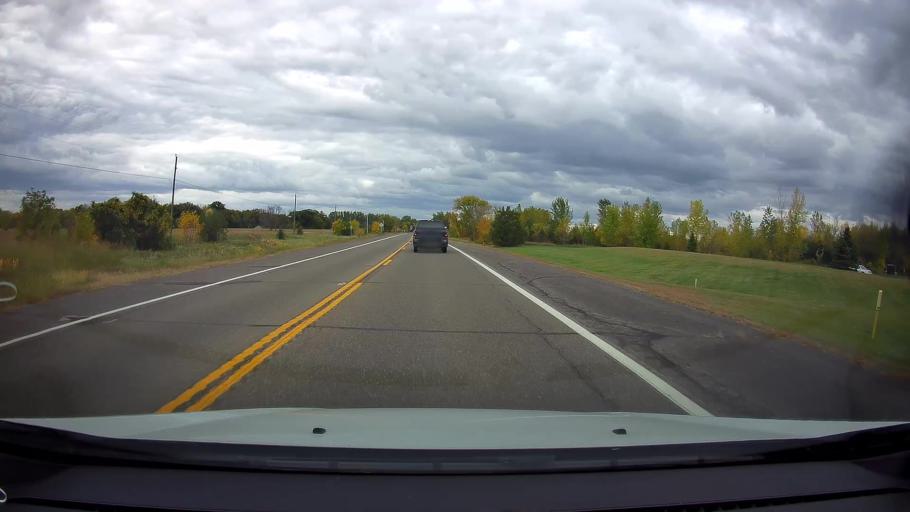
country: US
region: Minnesota
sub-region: Chisago County
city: Chisago City
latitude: 45.3520
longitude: -92.9117
